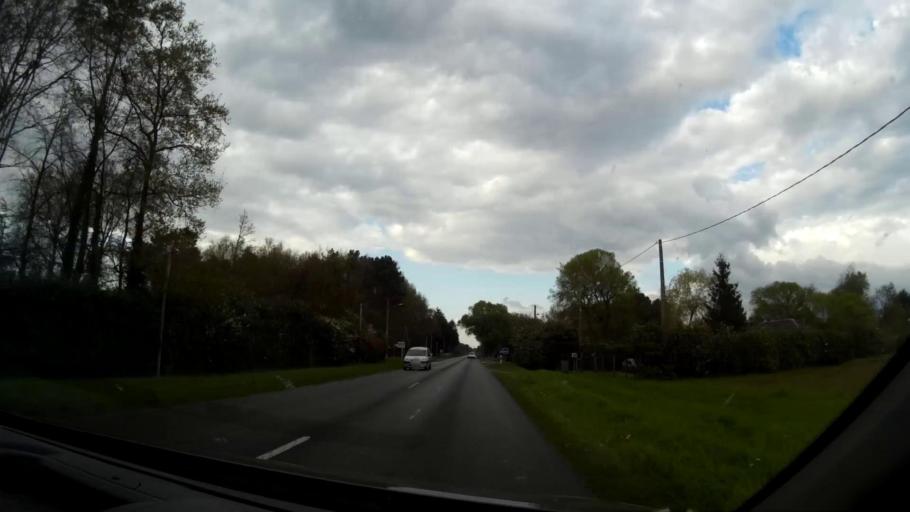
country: FR
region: Centre
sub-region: Departement du Loir-et-Cher
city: Contres
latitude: 47.4426
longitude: 1.4267
